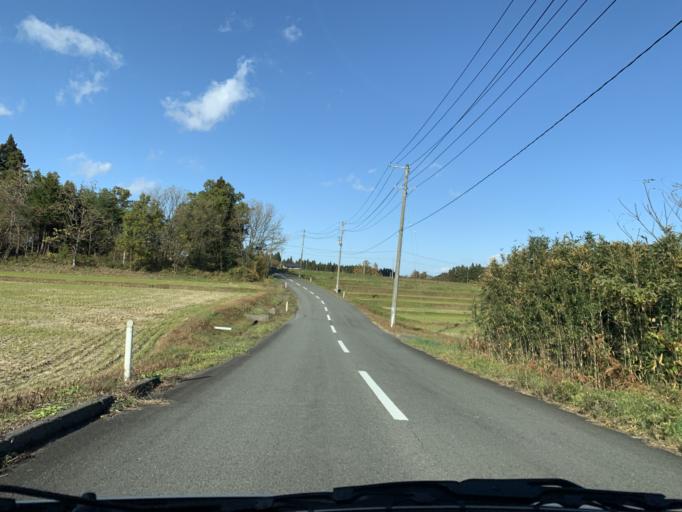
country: JP
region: Iwate
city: Mizusawa
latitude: 39.0649
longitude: 141.1126
